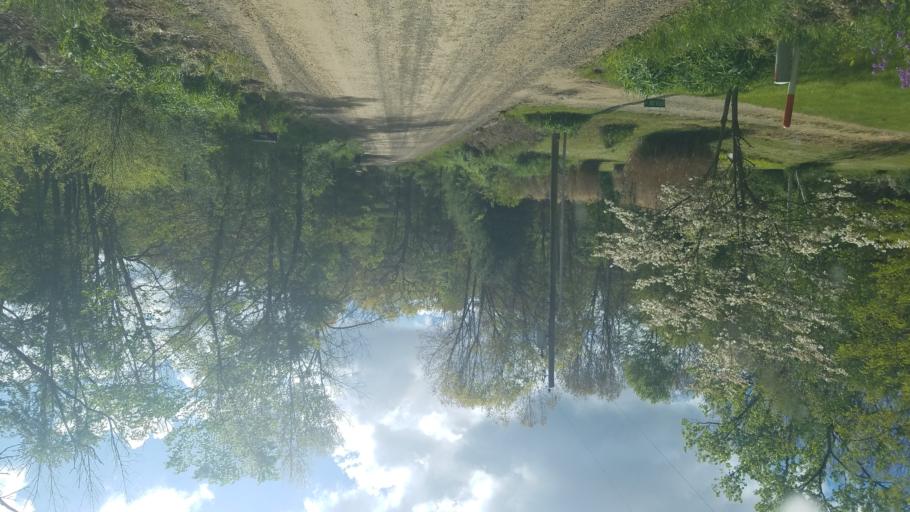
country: US
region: Ohio
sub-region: Knox County
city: Mount Vernon
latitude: 40.4464
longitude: -82.4365
